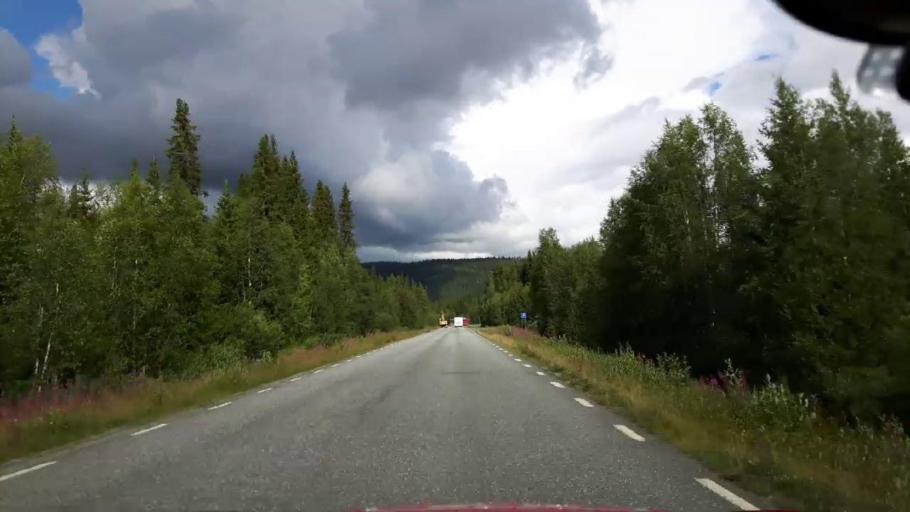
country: SE
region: Vaesterbotten
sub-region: Vilhelmina Kommun
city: Sjoberg
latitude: 64.9303
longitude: 15.8613
